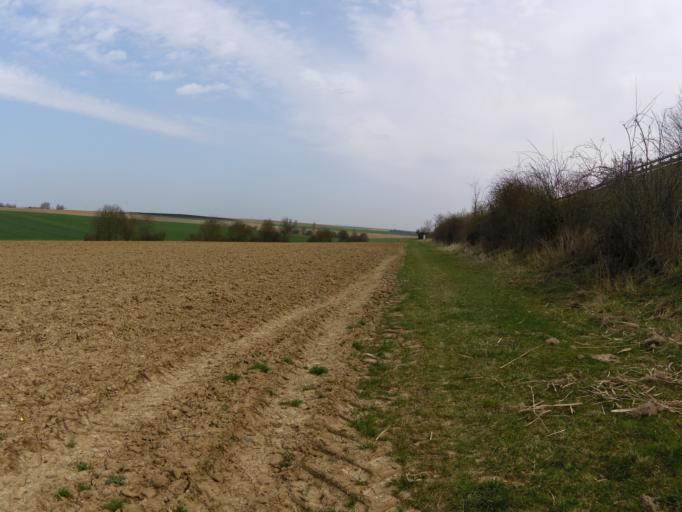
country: DE
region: Bavaria
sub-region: Regierungsbezirk Unterfranken
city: Biebelried
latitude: 49.7829
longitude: 10.1049
